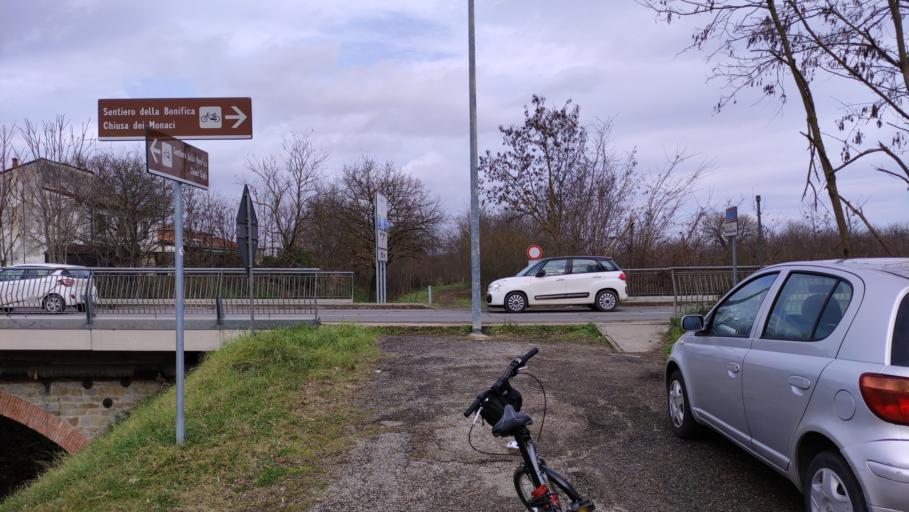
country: IT
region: Tuscany
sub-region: Province of Arezzo
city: Battifolle-Ruscello-Poggiola
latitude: 43.4609
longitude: 11.8199
